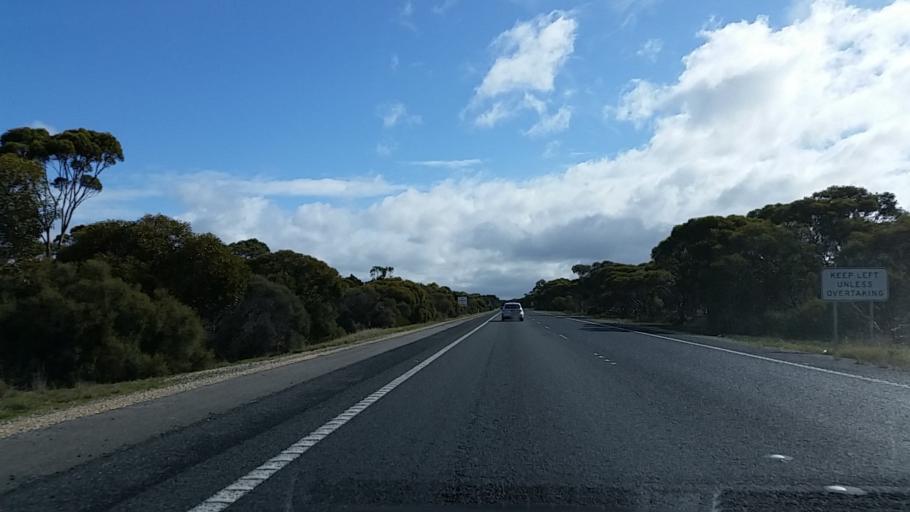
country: AU
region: South Australia
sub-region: Mount Barker
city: Callington
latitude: -35.1357
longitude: 139.1256
